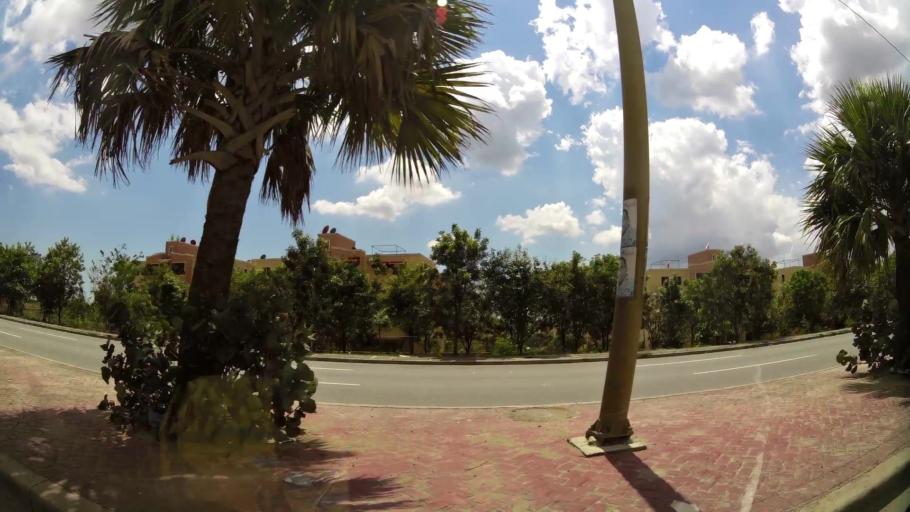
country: DO
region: Nacional
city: La Agustina
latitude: 18.5554
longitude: -69.9333
